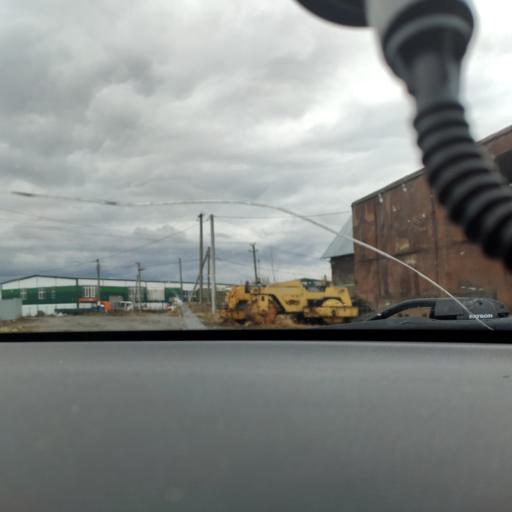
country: RU
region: Tatarstan
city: Osinovo
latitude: 55.8981
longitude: 48.9650
